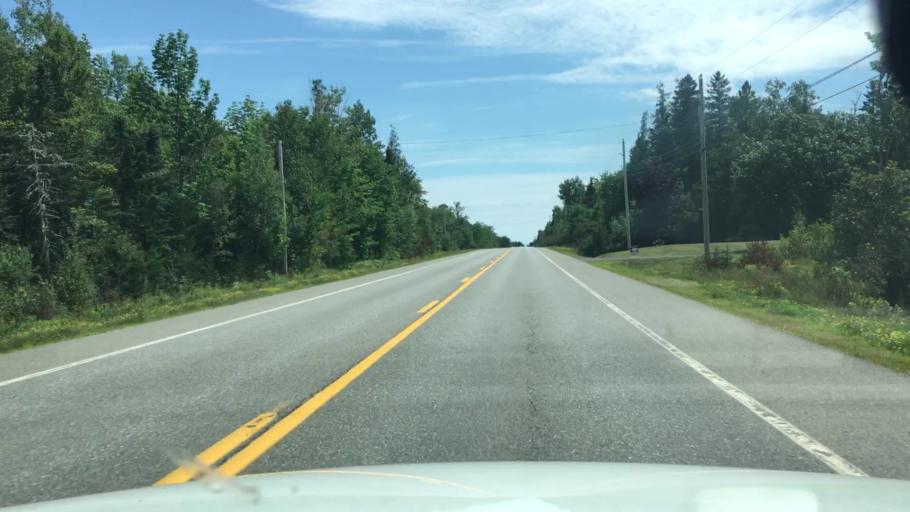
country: CA
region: New Brunswick
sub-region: Charlotte County
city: Saint Andrews
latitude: 45.0054
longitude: -67.0924
